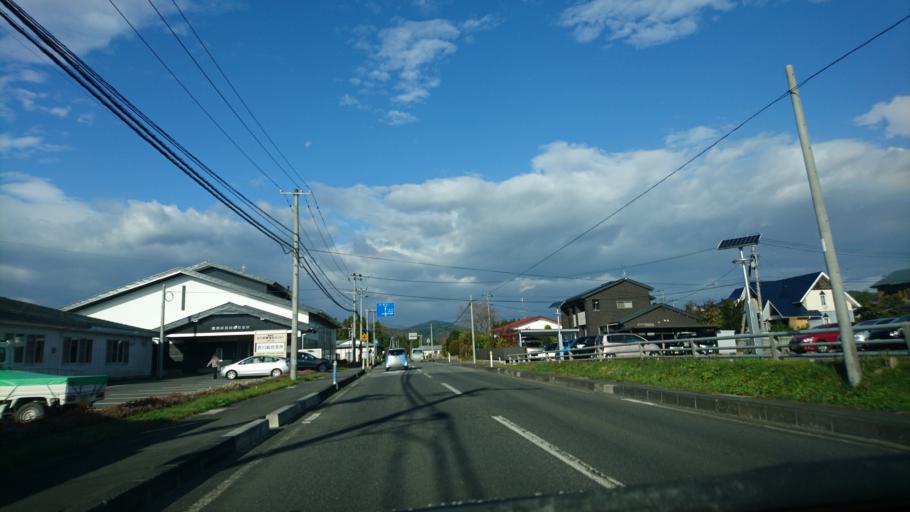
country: JP
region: Iwate
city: Mizusawa
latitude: 39.0392
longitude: 141.0642
